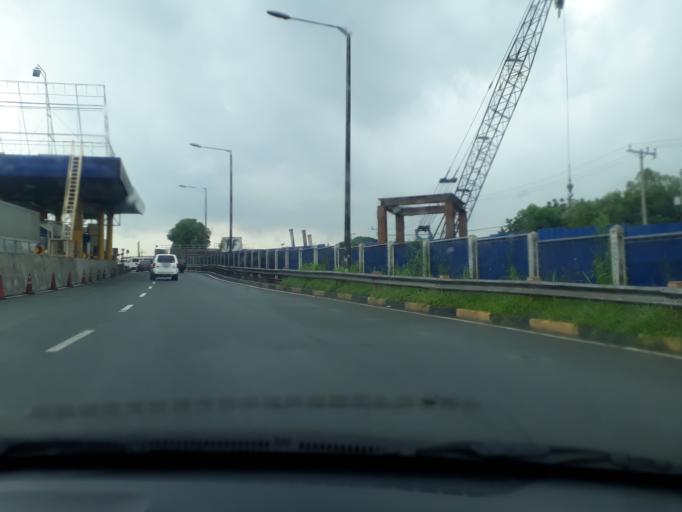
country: PH
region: Metro Manila
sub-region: Makati City
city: Makati City
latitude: 14.5138
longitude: 121.0340
